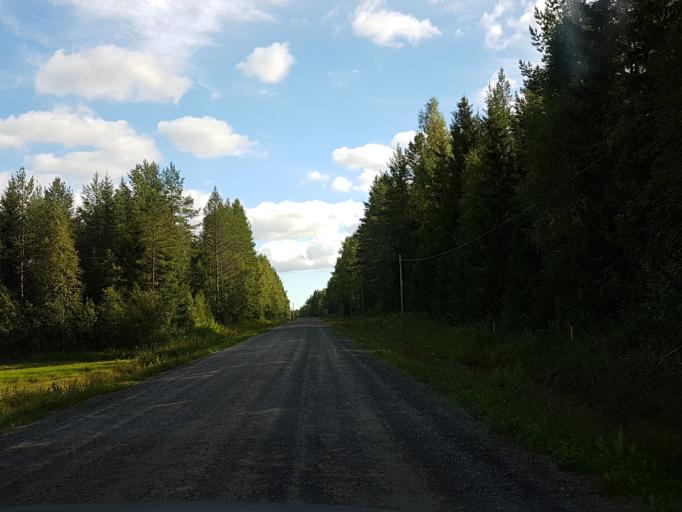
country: SE
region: Vaesterbotten
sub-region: Robertsfors Kommun
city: Robertsfors
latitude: 64.1692
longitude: 20.6463
